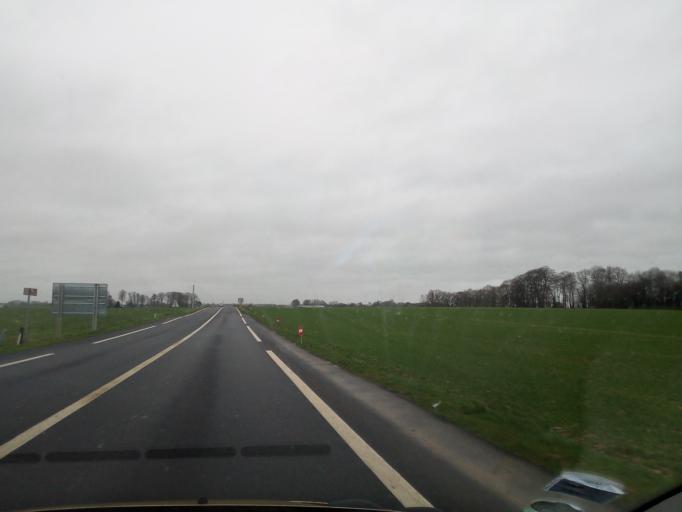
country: FR
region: Haute-Normandie
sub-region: Departement de la Seine-Maritime
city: Auzebosc
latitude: 49.5865
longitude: 0.7326
